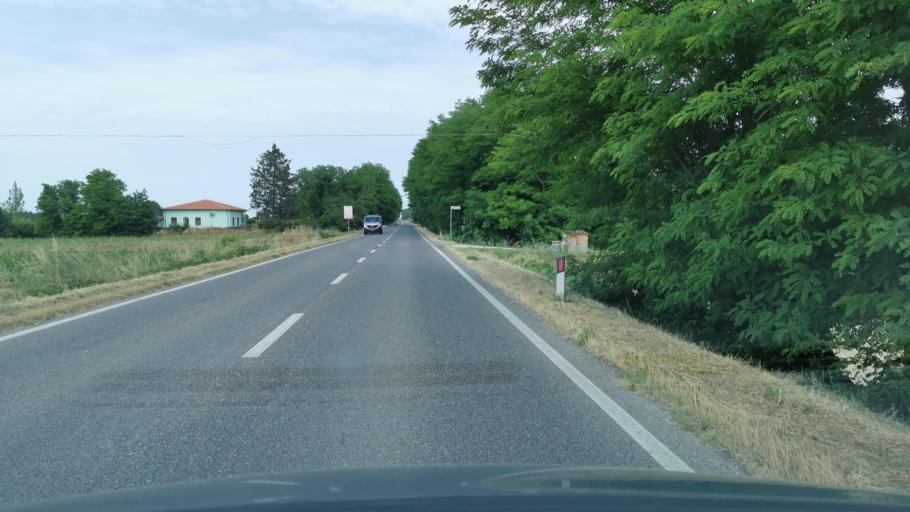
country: IT
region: Emilia-Romagna
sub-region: Provincia di Ravenna
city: Savarna-Conventella
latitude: 44.5299
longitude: 12.1187
